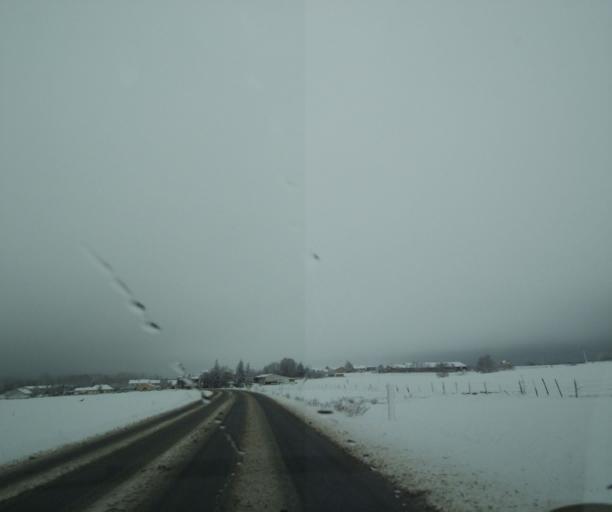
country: FR
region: Champagne-Ardenne
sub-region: Departement de la Haute-Marne
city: Wassy
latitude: 48.5214
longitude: 4.9332
